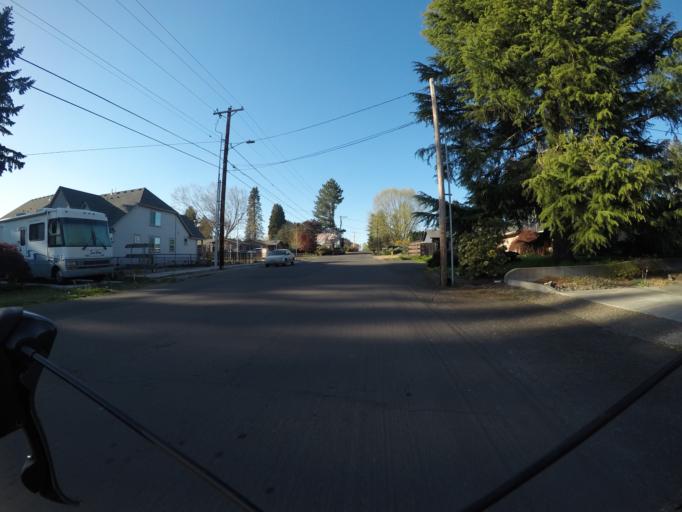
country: US
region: Oregon
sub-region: Washington County
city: Aloha
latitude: 45.4855
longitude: -122.8738
